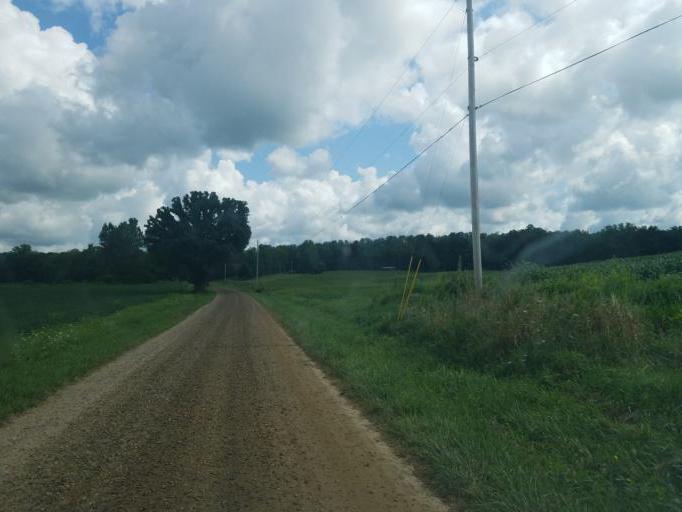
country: US
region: Ohio
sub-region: Knox County
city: Fredericktown
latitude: 40.4740
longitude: -82.6575
